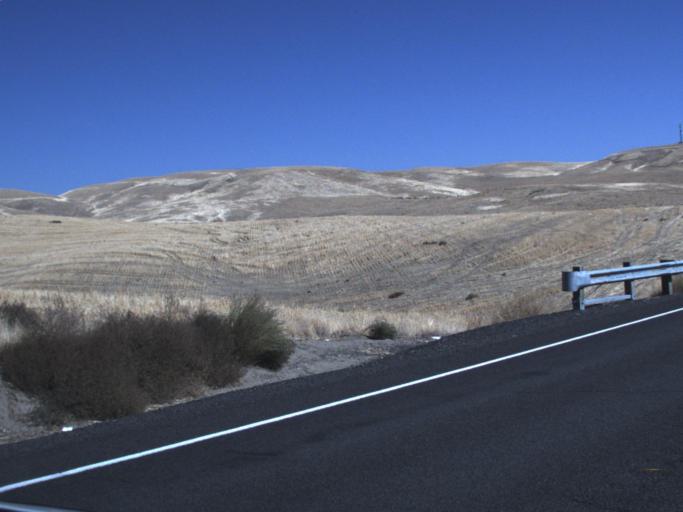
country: US
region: Washington
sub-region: Walla Walla County
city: Garrett
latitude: 46.2905
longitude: -118.5164
